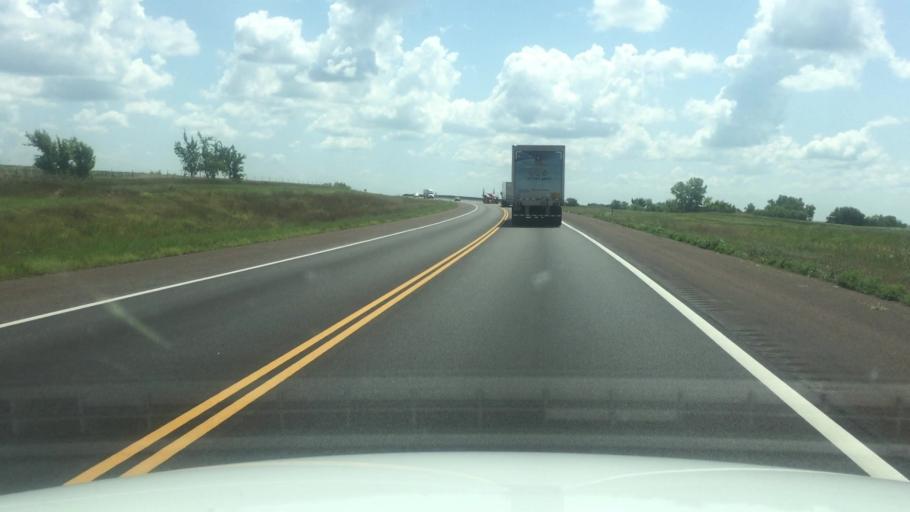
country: US
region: Kansas
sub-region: Nemaha County
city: Sabetha
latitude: 39.8707
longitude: -95.7780
